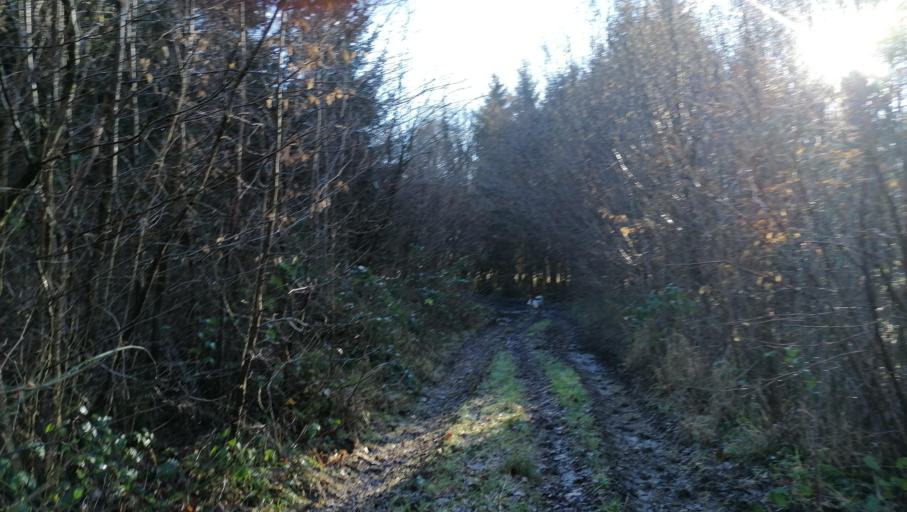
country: FR
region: Nord-Pas-de-Calais
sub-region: Departement du Nord
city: Recquignies
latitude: 50.1954
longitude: 4.0660
